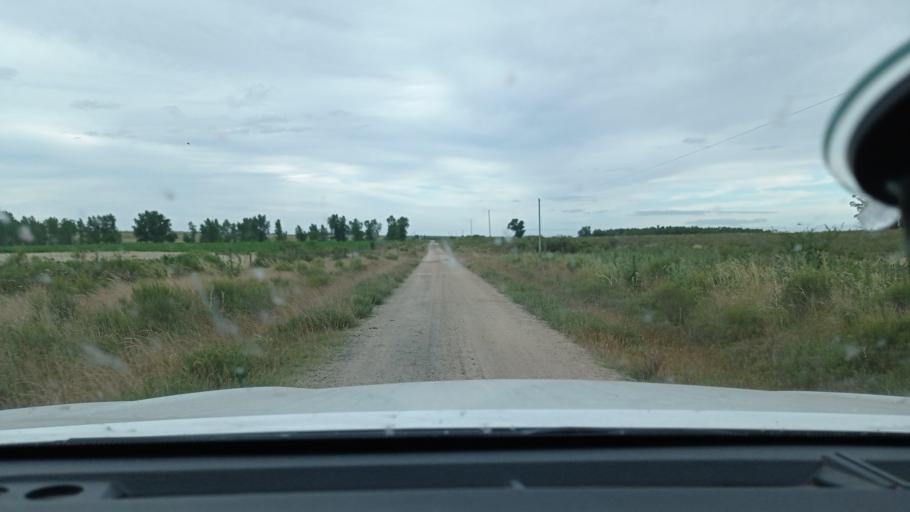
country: UY
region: Florida
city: Casupa
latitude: -34.1304
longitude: -55.7780
